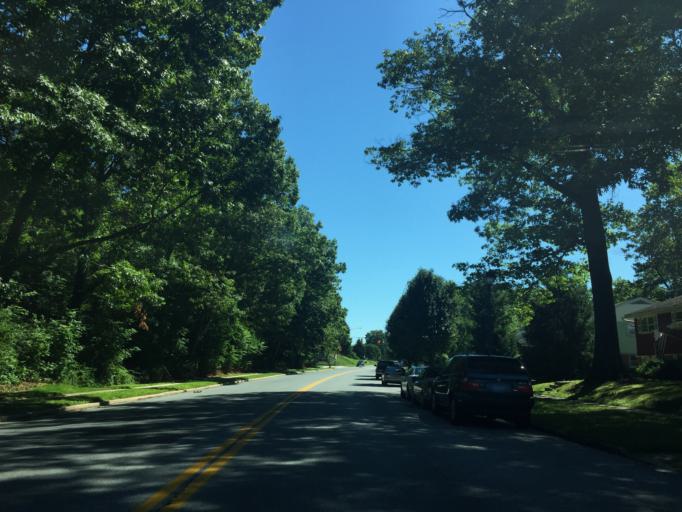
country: US
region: Maryland
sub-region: Baltimore County
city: Timonium
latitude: 39.4315
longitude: -76.6180
